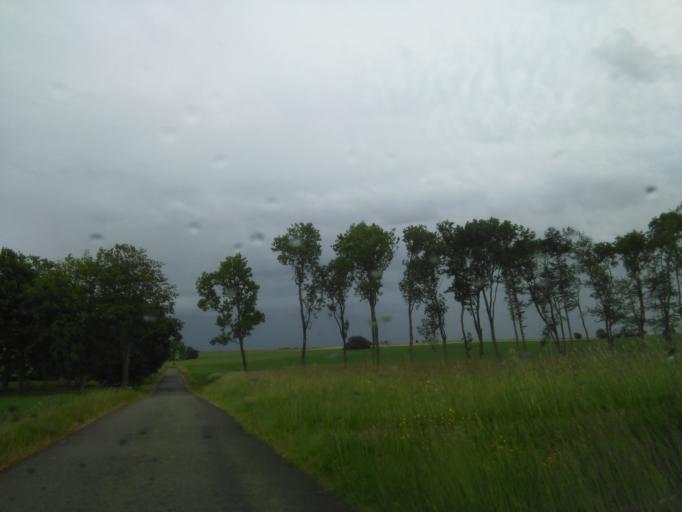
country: DK
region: Capital Region
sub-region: Bornholm Kommune
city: Nexo
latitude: 55.0949
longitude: 15.1404
